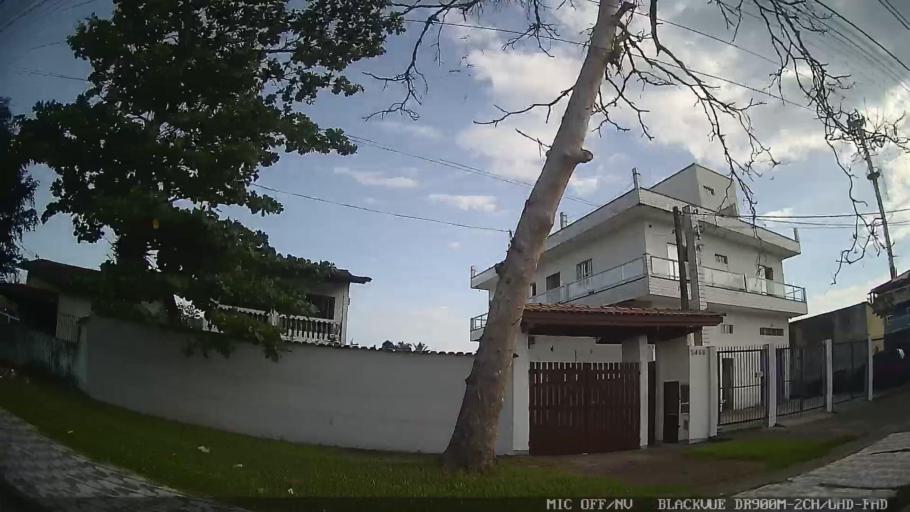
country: BR
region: Sao Paulo
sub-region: Bertioga
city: Bertioga
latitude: -23.8149
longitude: -46.0809
